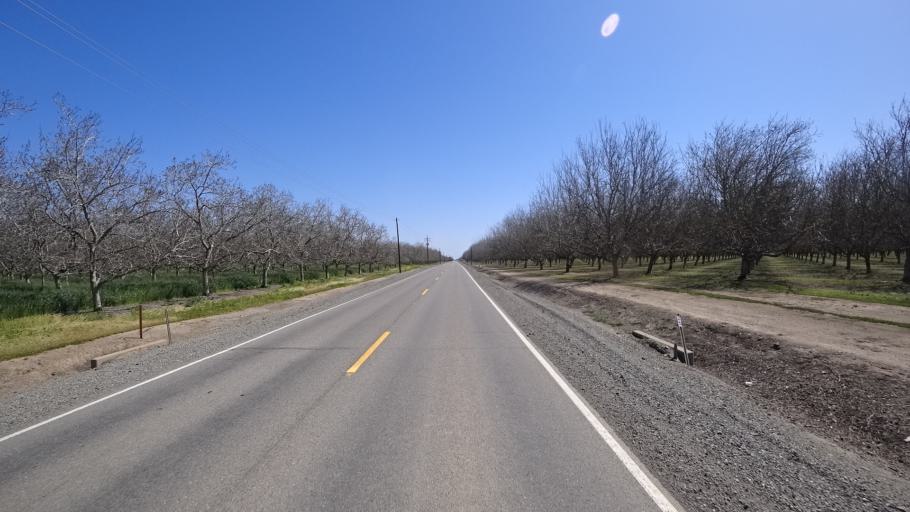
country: US
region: California
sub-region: Glenn County
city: Willows
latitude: 39.4644
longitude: -121.9849
